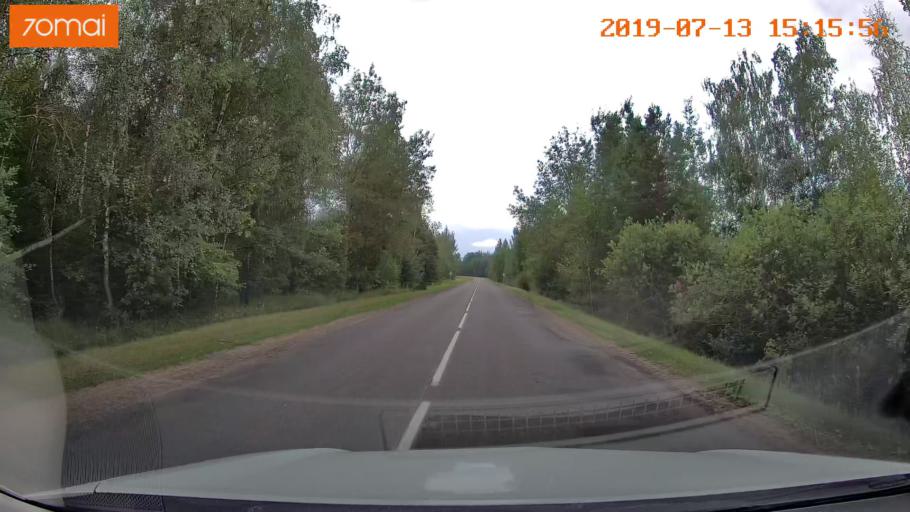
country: BY
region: Mogilev
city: Hlusha
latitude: 53.1131
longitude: 28.8290
